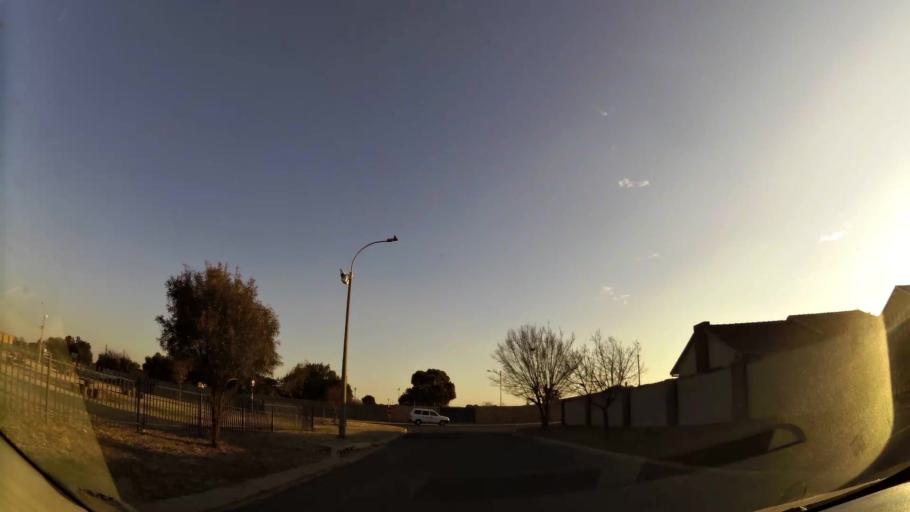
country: ZA
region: Gauteng
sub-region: West Rand District Municipality
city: Randfontein
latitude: -26.2074
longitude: 27.6550
